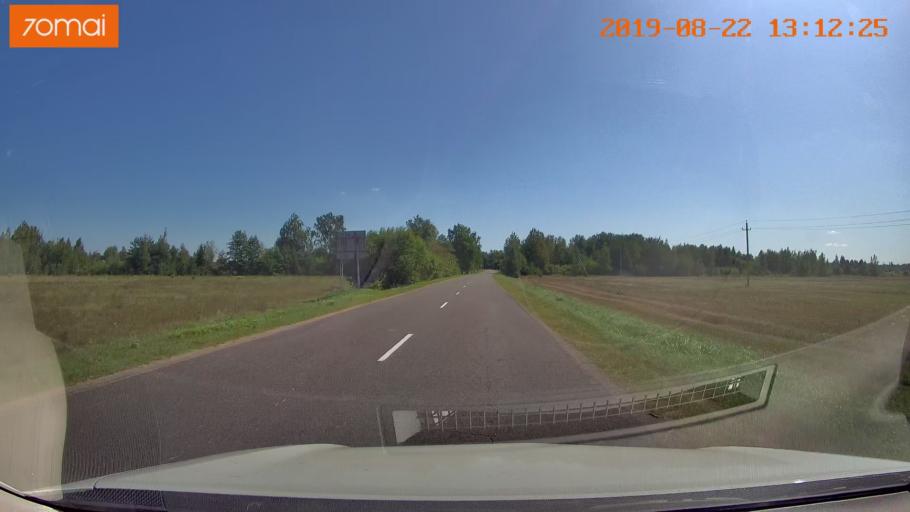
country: BY
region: Minsk
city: Prawdzinski
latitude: 53.2697
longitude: 27.8631
